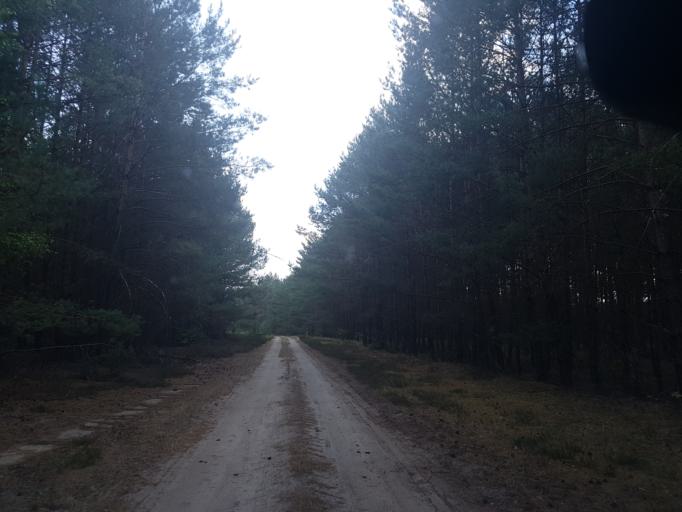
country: DE
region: Brandenburg
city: Treuenbrietzen
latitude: 52.0488
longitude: 12.8486
